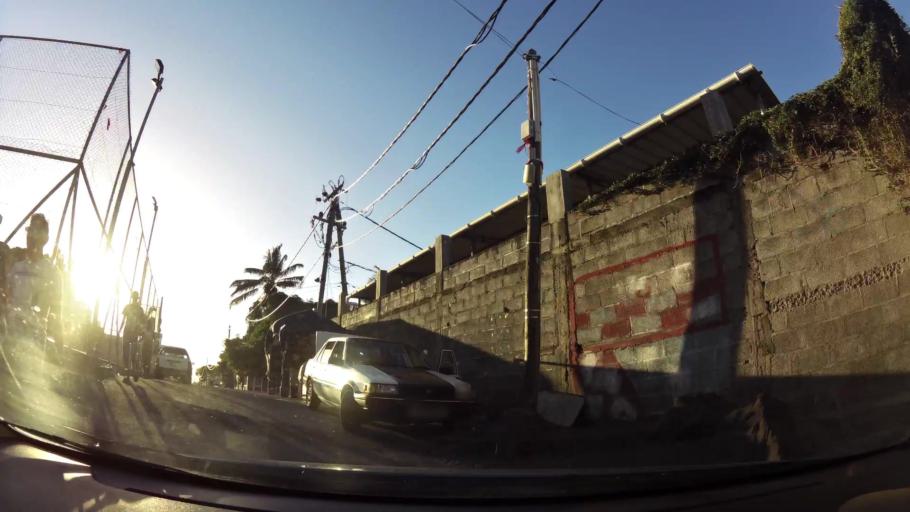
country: MU
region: Port Louis
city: Port Louis
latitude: -20.1773
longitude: 57.5131
